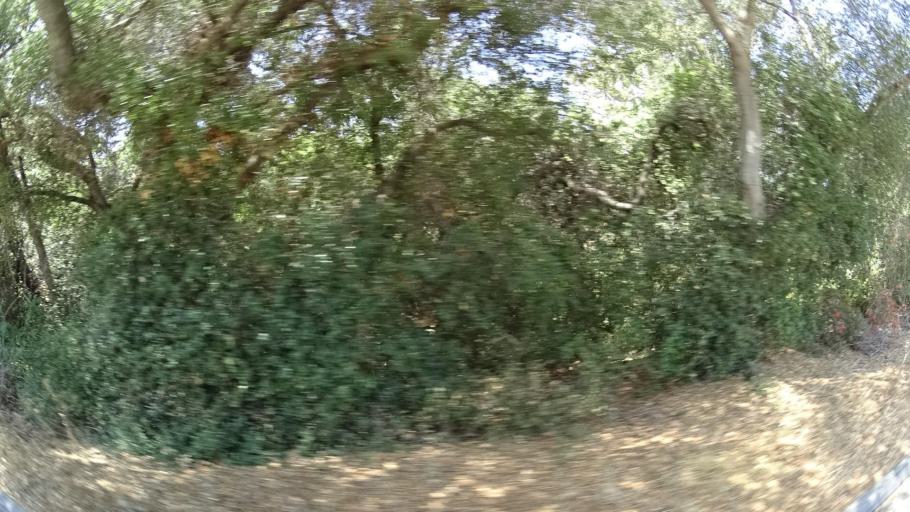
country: US
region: California
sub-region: San Diego County
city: Bonsall
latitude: 33.3129
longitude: -117.2185
